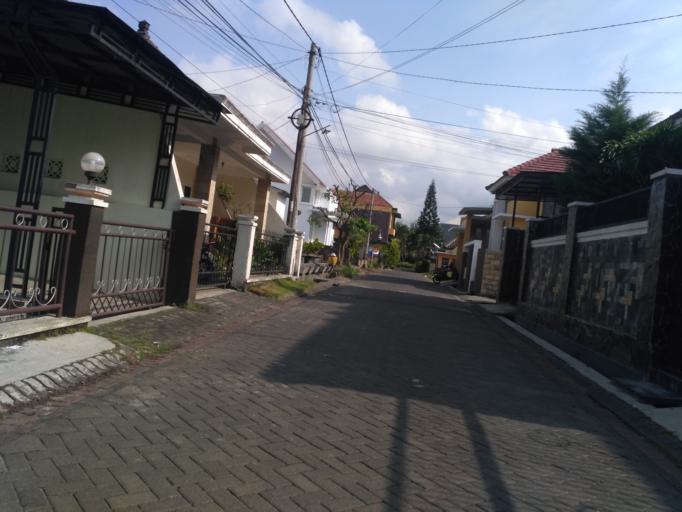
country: ID
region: East Java
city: Malang
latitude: -7.9368
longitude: 112.6134
